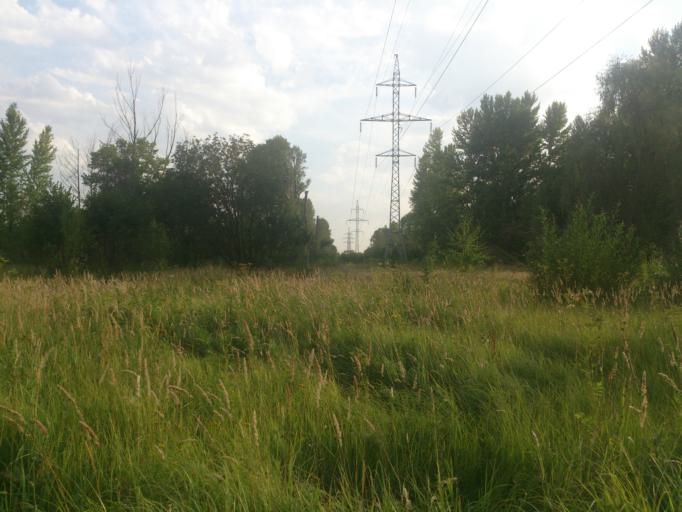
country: RU
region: Ulyanovsk
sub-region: Ulyanovskiy Rayon
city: Ulyanovsk
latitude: 54.2981
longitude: 48.3537
